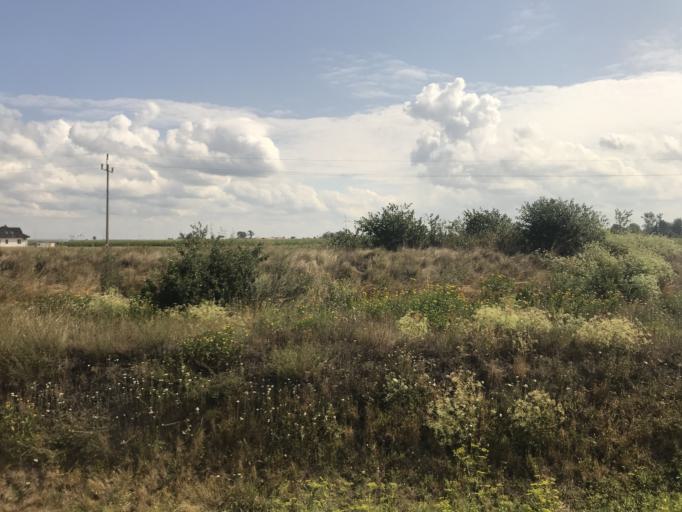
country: PL
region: Kujawsko-Pomorskie
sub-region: Powiat inowroclawski
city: Zlotniki Kujawskie
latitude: 52.9171
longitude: 18.1326
